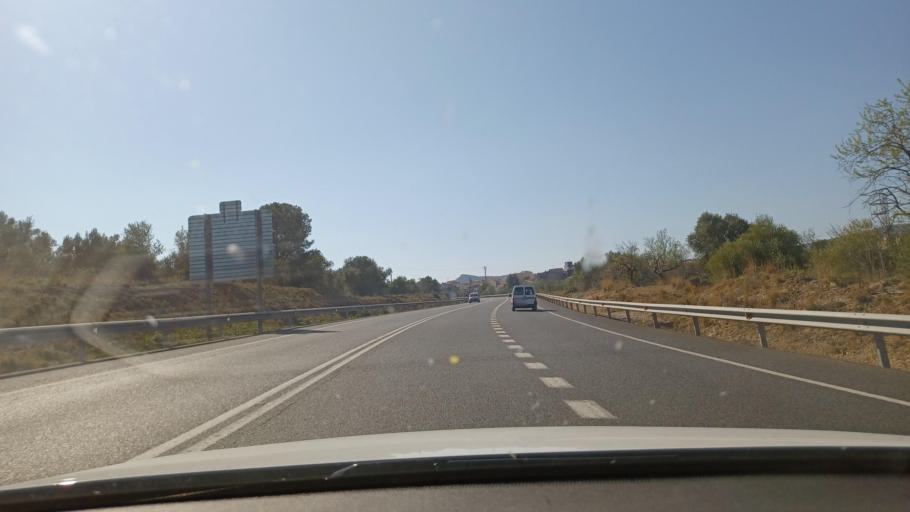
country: ES
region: Catalonia
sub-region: Provincia de Tarragona
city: El Perello
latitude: 40.8768
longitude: 0.7170
